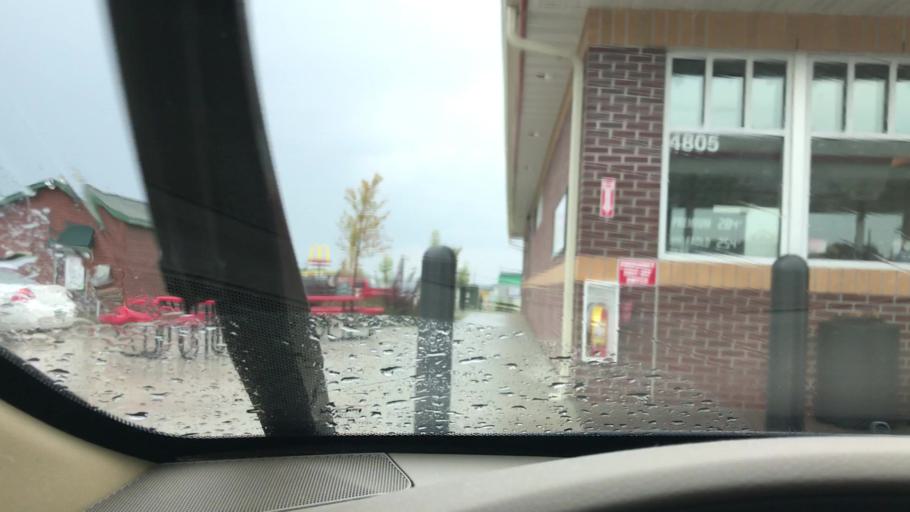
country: US
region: Minnesota
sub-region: Saint Louis County
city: Hermantown
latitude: 46.8232
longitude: -92.1869
